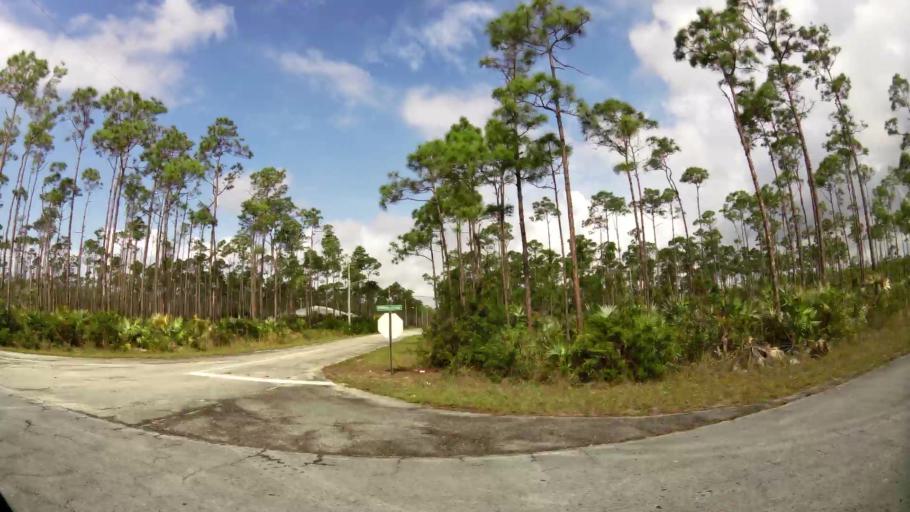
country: BS
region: Freeport
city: Lucaya
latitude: 26.5805
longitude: -78.5494
